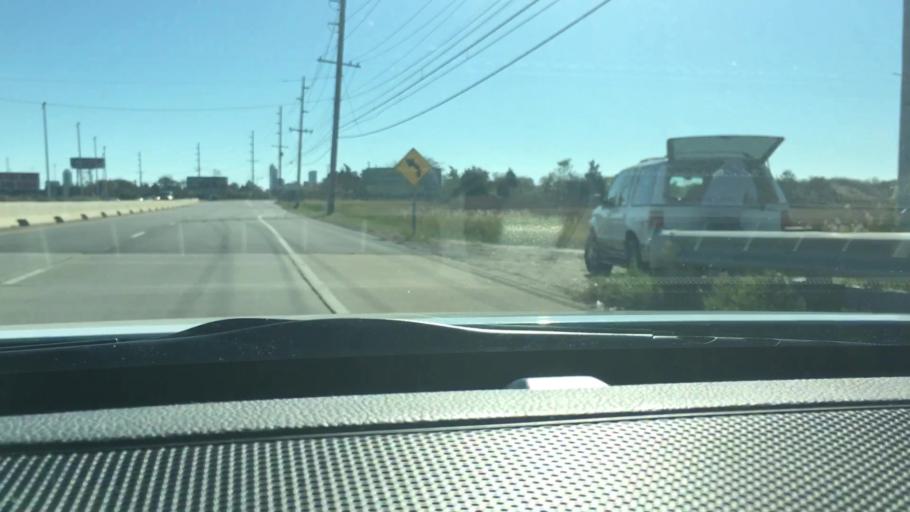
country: US
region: New Jersey
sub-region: Atlantic County
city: Atlantic City
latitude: 39.3813
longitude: -74.4591
